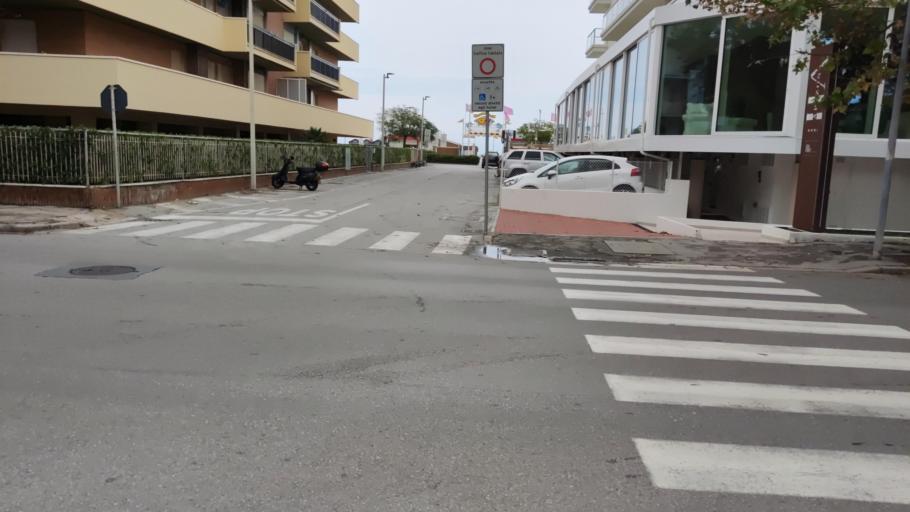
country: IT
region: Emilia-Romagna
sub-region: Provincia di Rimini
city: Riccione
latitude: 44.0084
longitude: 12.6525
